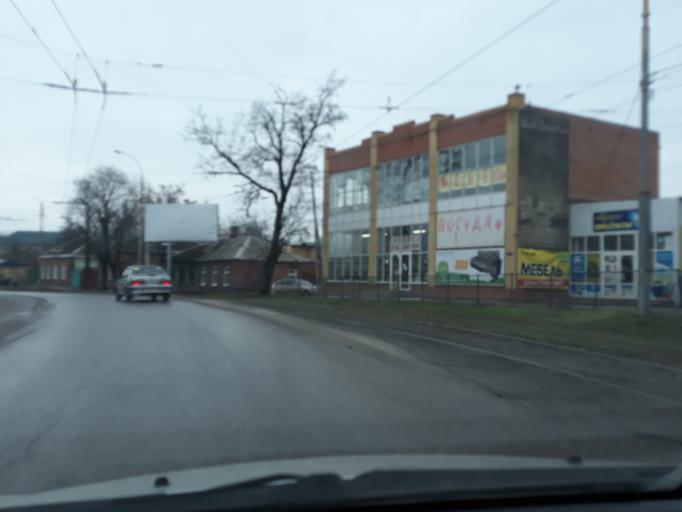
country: RU
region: Rostov
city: Taganrog
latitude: 47.2268
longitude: 38.9173
